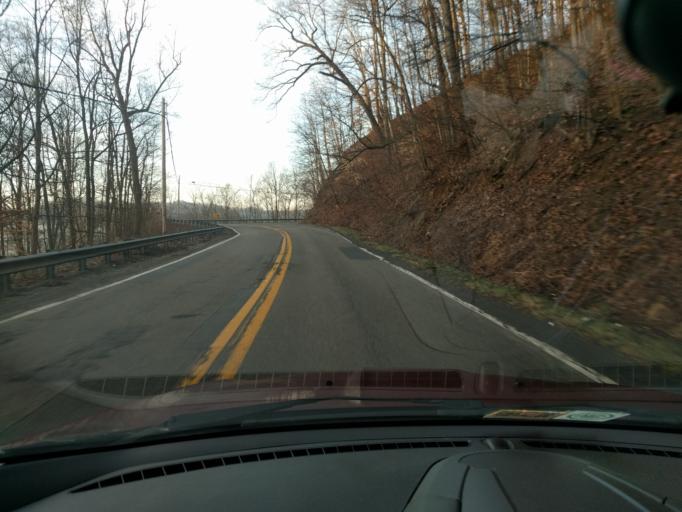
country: US
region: West Virginia
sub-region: Fayette County
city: Ansted
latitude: 38.1432
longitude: -81.1573
